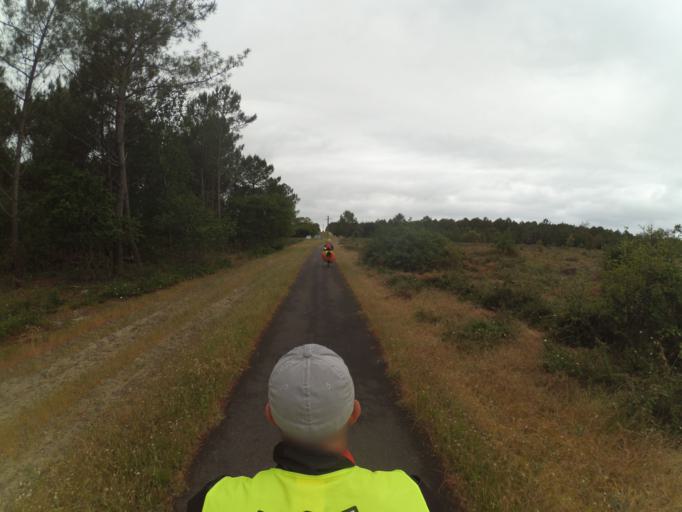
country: FR
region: Aquitaine
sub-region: Departement des Landes
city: Mimizan
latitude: 44.2191
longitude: -1.2799
